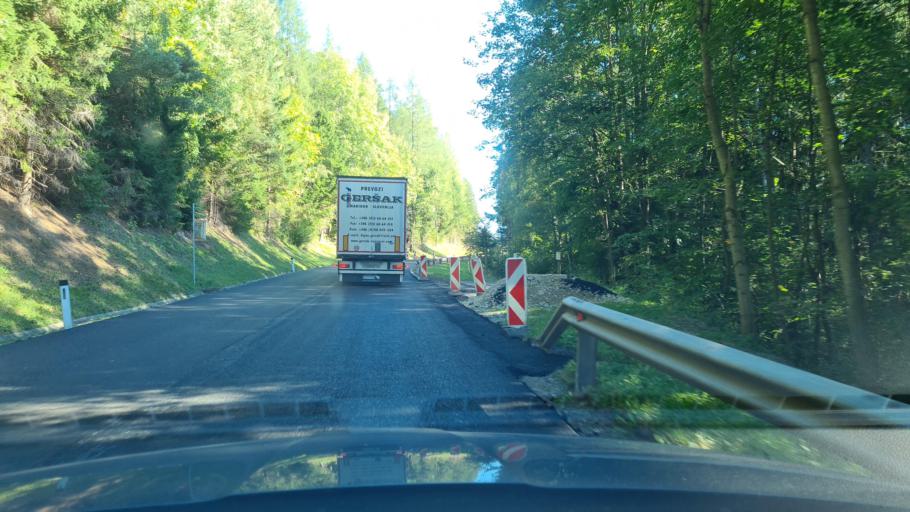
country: AT
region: Styria
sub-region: Politischer Bezirk Graz-Umgebung
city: Schrems bei Frohnleiten
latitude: 47.2780
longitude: 15.3975
